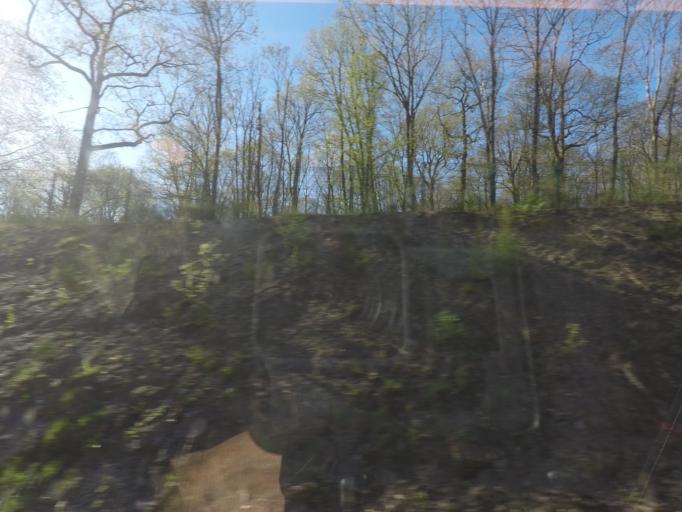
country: BE
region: Wallonia
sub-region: Province de Namur
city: Rochefort
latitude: 50.2486
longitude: 5.2517
